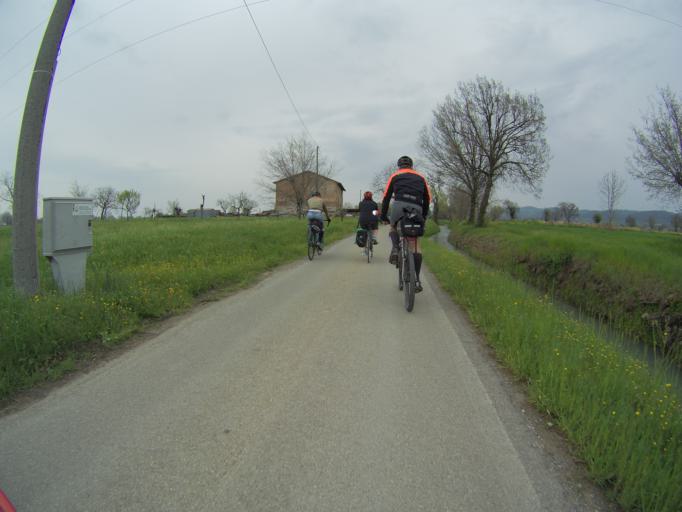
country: IT
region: Emilia-Romagna
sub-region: Provincia di Reggio Emilia
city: San Polo d'Enza
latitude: 44.6526
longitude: 10.4359
